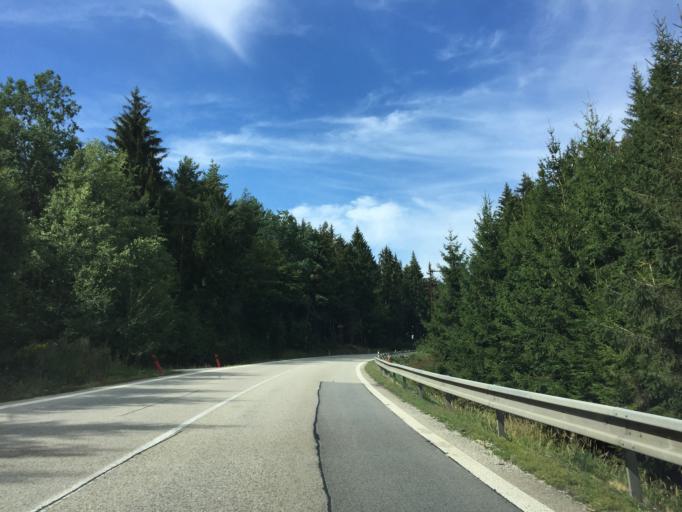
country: CZ
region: Central Bohemia
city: Votice
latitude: 49.5876
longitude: 14.6618
